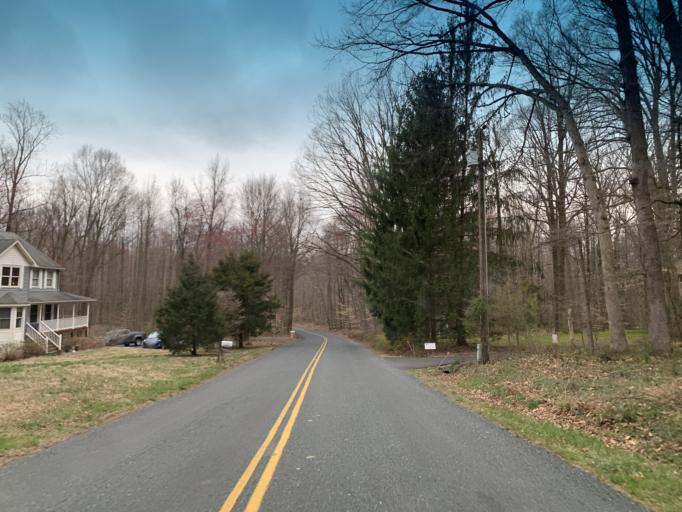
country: US
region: Maryland
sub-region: Harford County
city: Aberdeen
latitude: 39.5240
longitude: -76.2097
